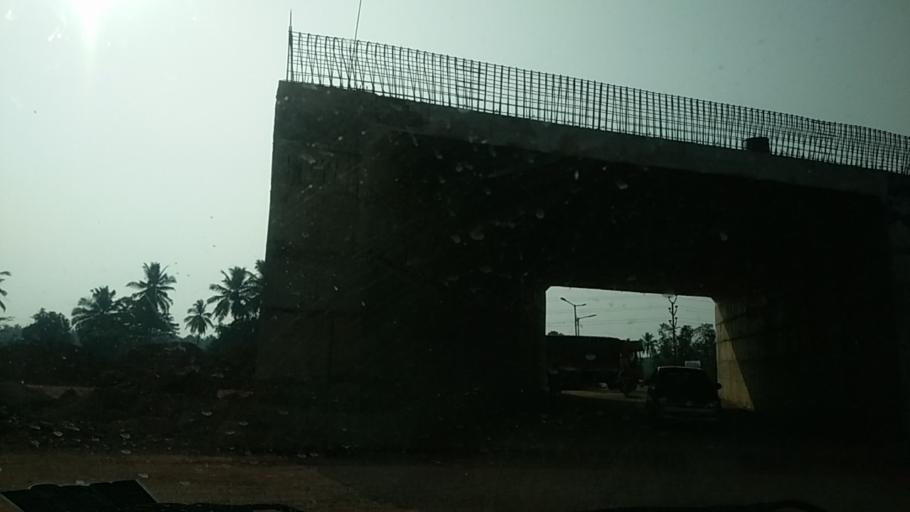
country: IN
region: Goa
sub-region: South Goa
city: Raia
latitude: 15.3071
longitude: 73.9447
